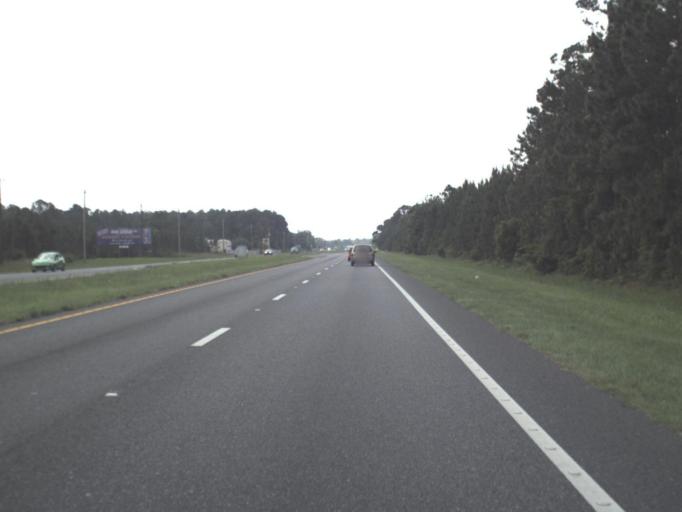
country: US
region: Florida
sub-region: Putnam County
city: Palatka
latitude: 29.6811
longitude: -81.6613
